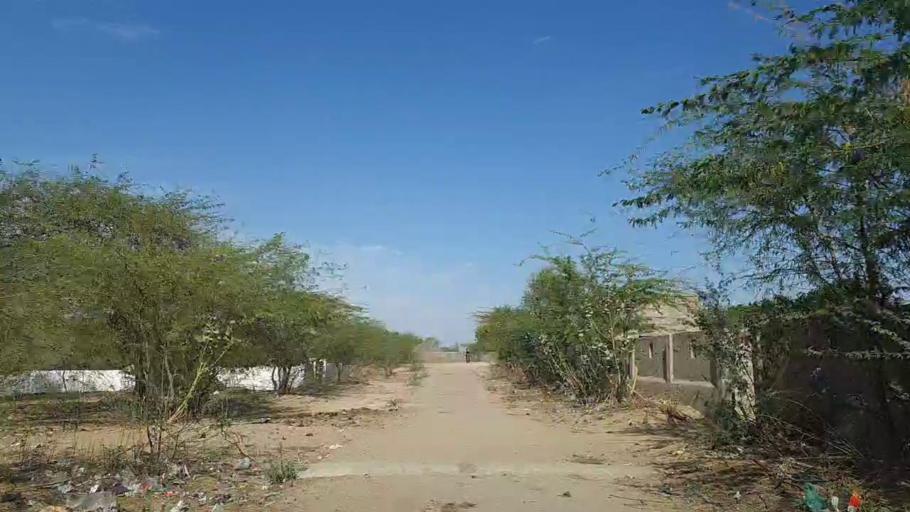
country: PK
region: Sindh
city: Naukot
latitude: 24.8203
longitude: 69.5402
